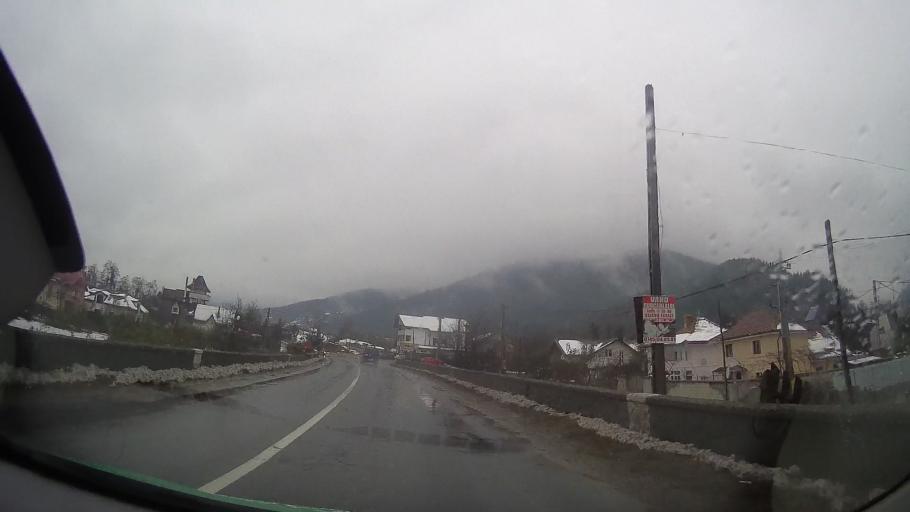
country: RO
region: Neamt
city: Viisoara
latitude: 46.9314
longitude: 26.2193
